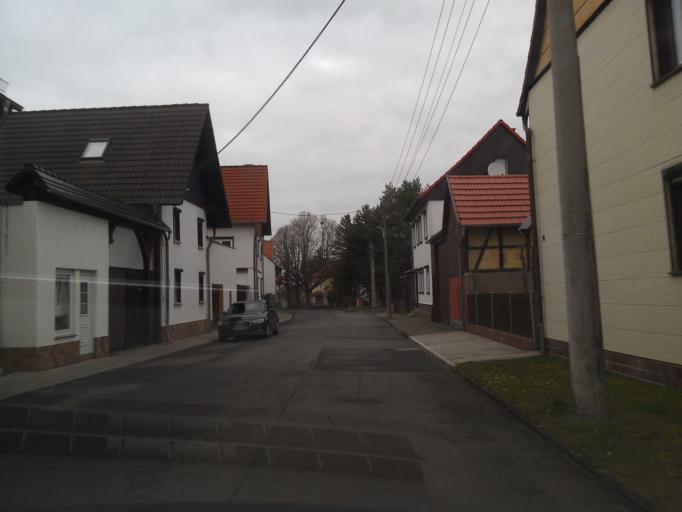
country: DE
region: Thuringia
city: Bufleben
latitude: 50.9987
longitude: 10.7392
